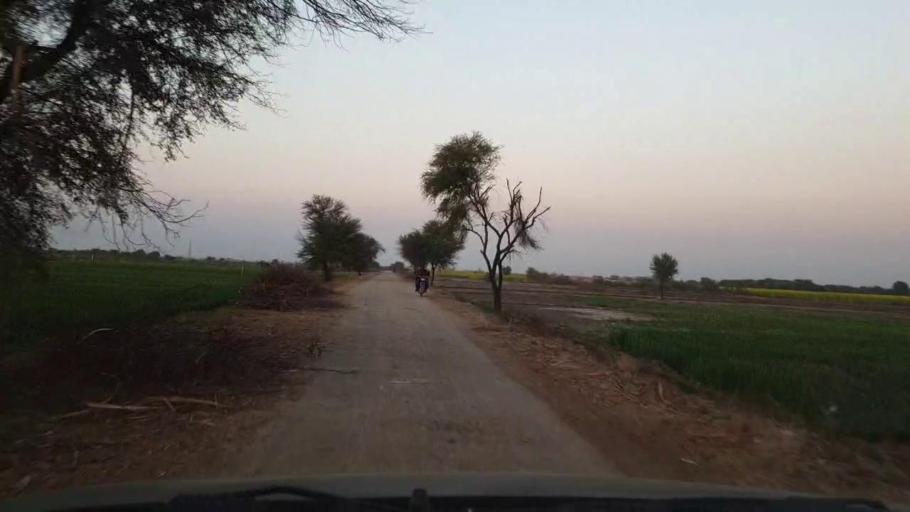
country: PK
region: Sindh
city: Jhol
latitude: 25.9426
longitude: 68.9732
